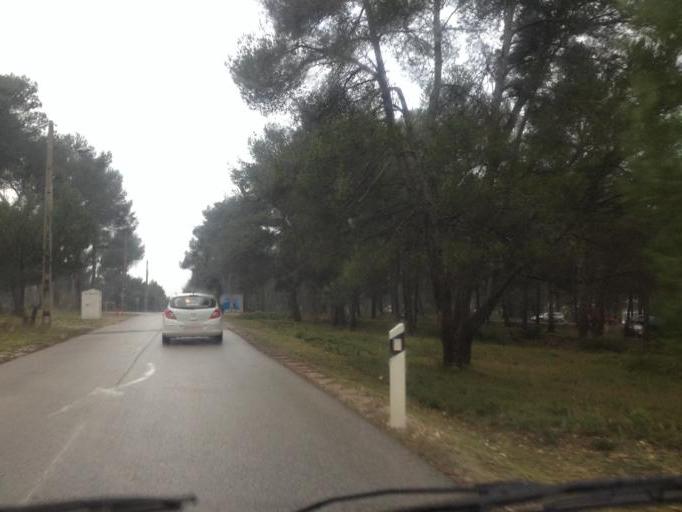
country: FR
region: Provence-Alpes-Cote d'Azur
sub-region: Departement des Bouches-du-Rhone
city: Ventabren
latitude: 43.4902
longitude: 5.3367
